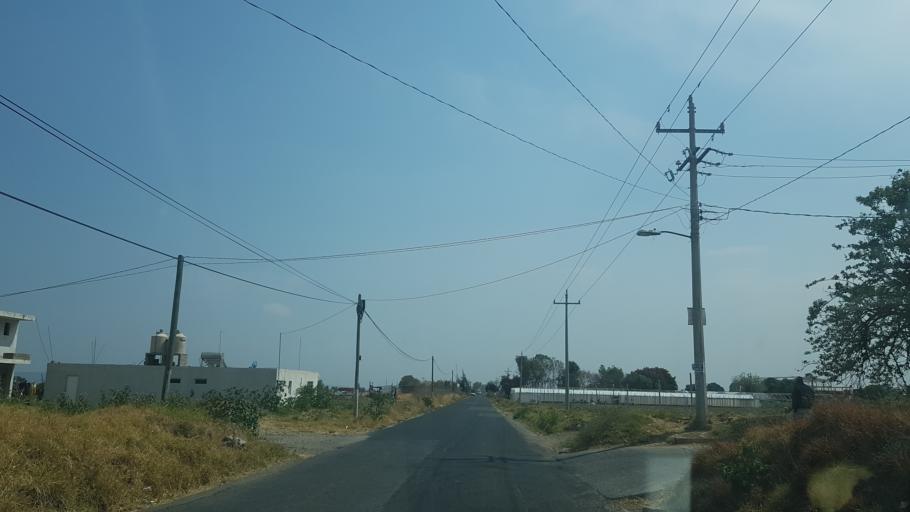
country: MX
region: Puebla
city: San Juan Tianguismanalco
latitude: 18.9421
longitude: -98.4540
